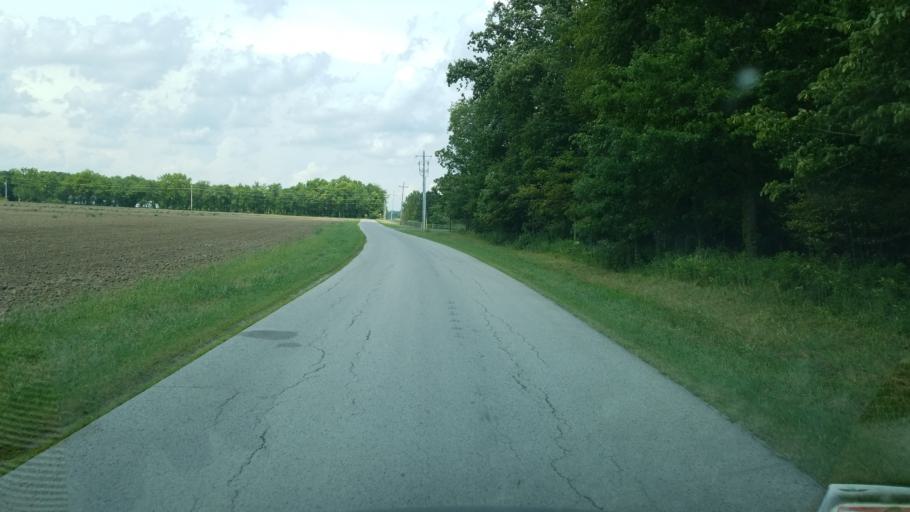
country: US
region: Ohio
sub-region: Hancock County
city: Arlington
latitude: 40.9528
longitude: -83.5412
